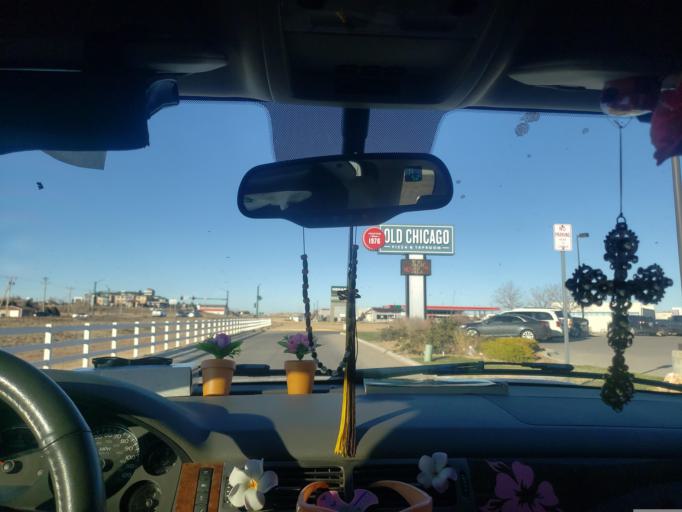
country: US
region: Kansas
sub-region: Finney County
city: Garden City
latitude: 37.9734
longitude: -100.8381
